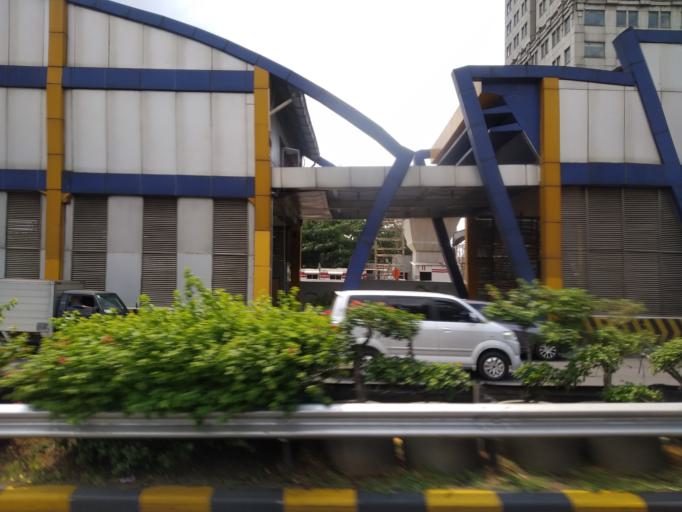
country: ID
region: Jakarta Raya
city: Jakarta
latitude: -6.2433
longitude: 106.8596
